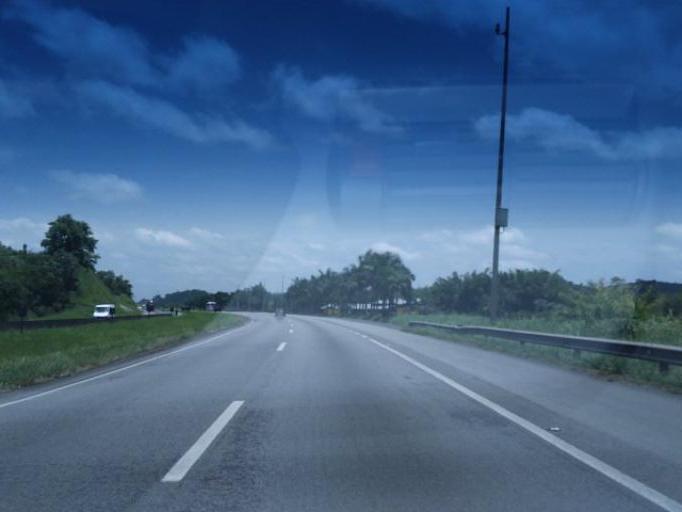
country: BR
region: Sao Paulo
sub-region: Registro
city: Registro
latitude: -24.4227
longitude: -47.7778
